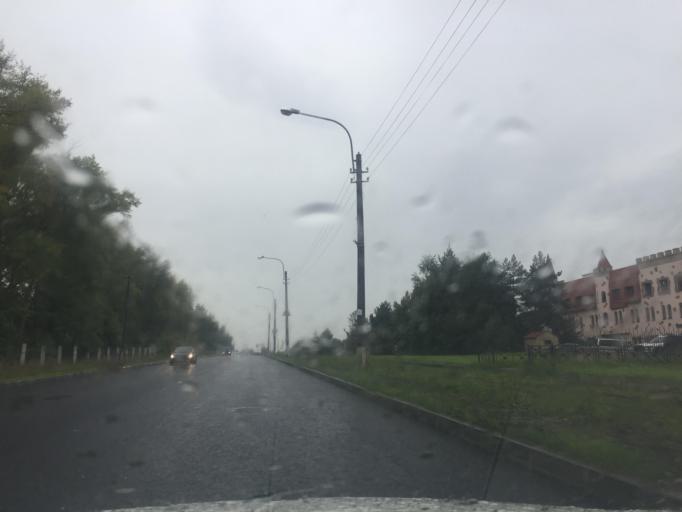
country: RU
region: St.-Petersburg
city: Pushkin
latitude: 59.7327
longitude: 30.3781
